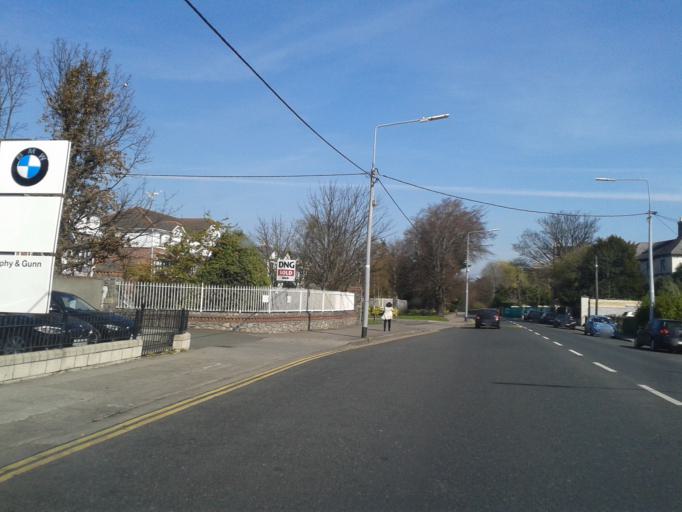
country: IE
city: Milltown
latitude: 53.3148
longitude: -6.2460
